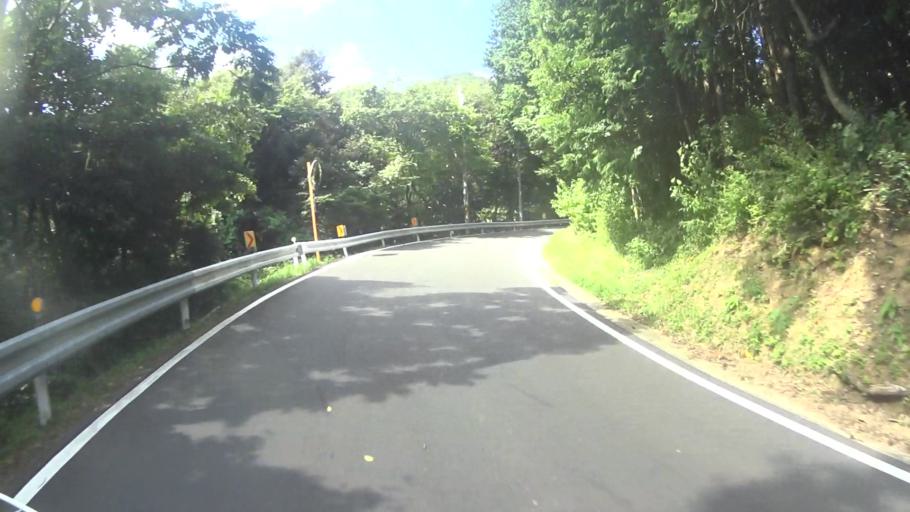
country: JP
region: Kyoto
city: Miyazu
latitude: 35.7455
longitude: 135.2449
